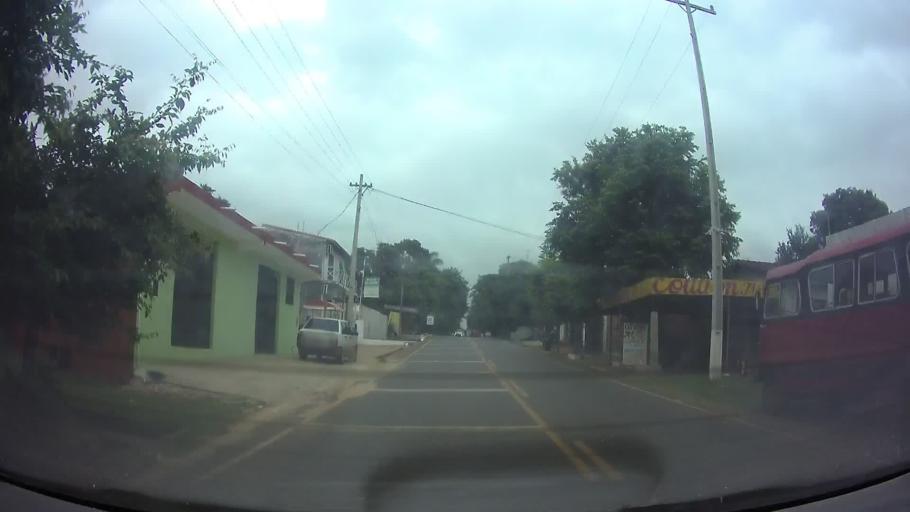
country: PY
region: Paraguari
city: Carapegua
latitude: -25.7699
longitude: -57.2463
